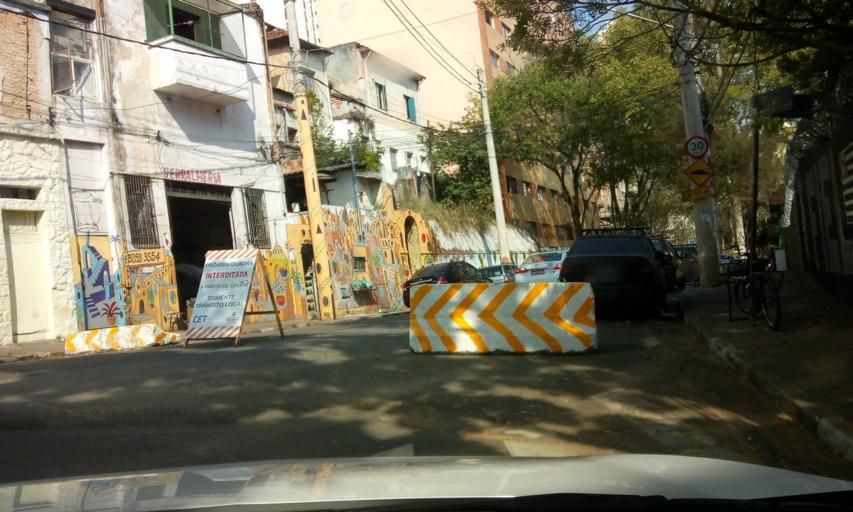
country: BR
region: Sao Paulo
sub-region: Sao Paulo
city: Sao Paulo
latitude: -23.5584
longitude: -46.6485
